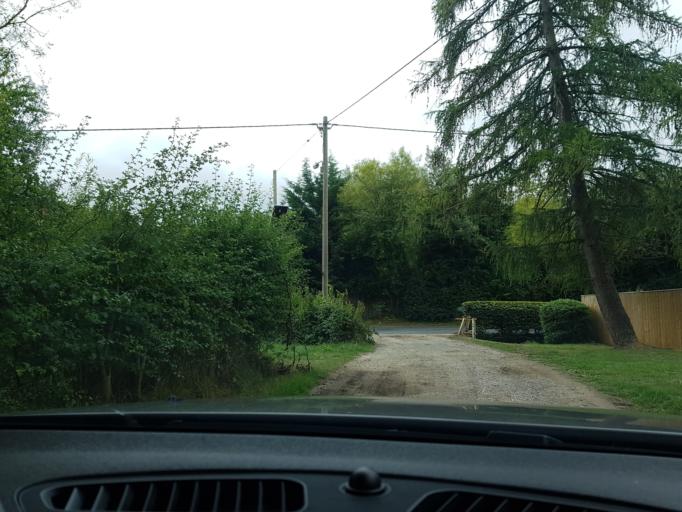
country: GB
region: England
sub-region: Wiltshire
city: Ramsbury
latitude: 51.4422
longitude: -1.5929
